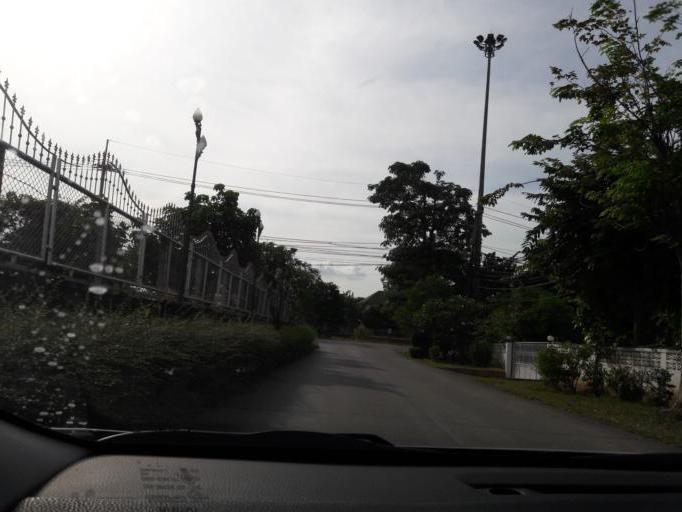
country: TH
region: Ang Thong
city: Ang Thong
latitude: 14.5828
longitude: 100.4449
